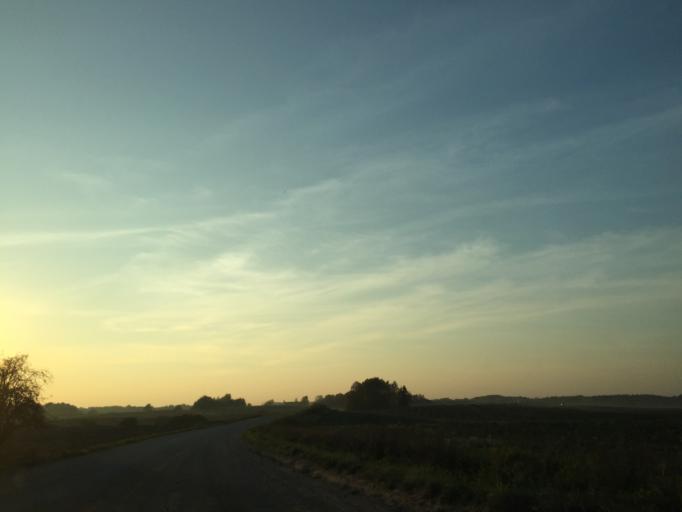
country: LV
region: Priekule
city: Priekule
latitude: 56.4732
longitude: 21.6455
